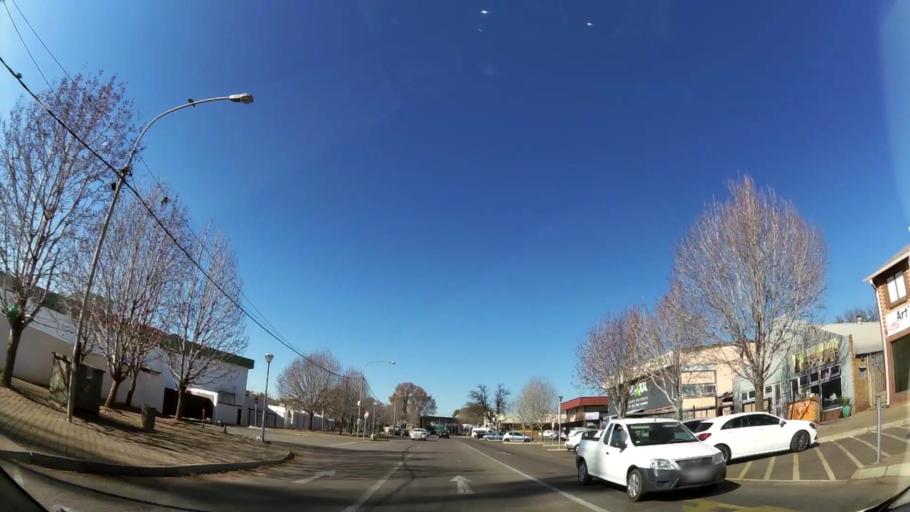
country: ZA
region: Gauteng
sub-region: City of Tshwane Metropolitan Municipality
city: Centurion
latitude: -25.8286
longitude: 28.2044
